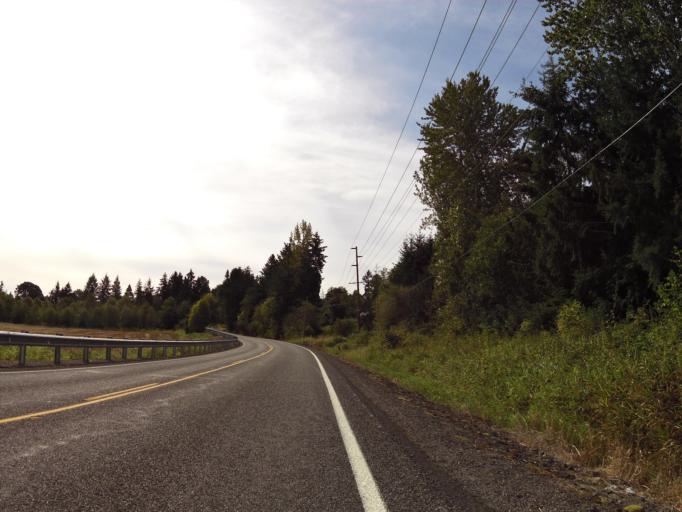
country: US
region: Washington
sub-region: Lewis County
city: Chehalis
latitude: 46.6366
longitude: -122.9714
